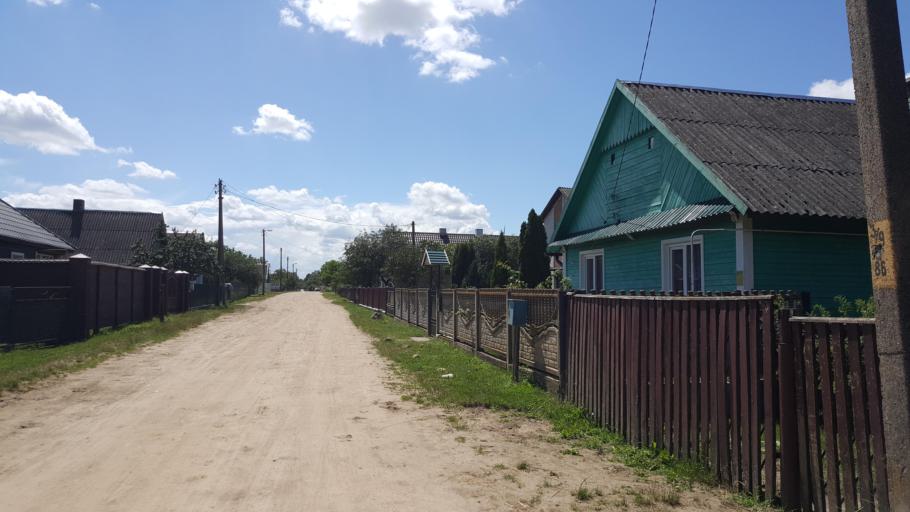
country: BY
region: Brest
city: Kamyanyets
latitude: 52.3267
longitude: 23.9138
